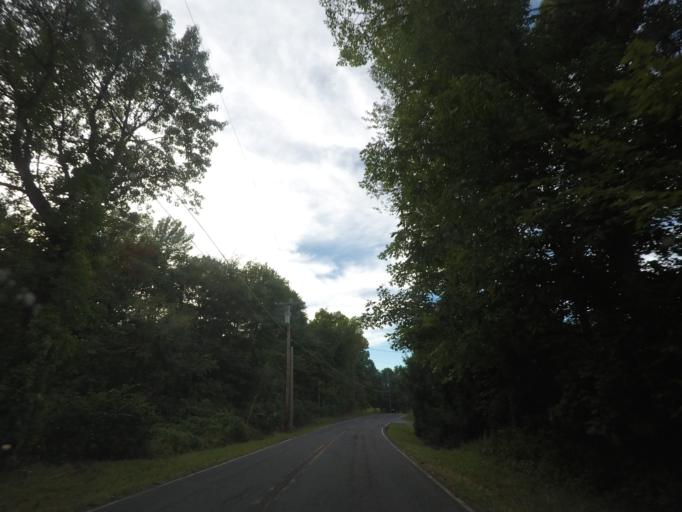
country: US
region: New York
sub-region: Rensselaer County
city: East Greenbush
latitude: 42.6138
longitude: -73.6777
